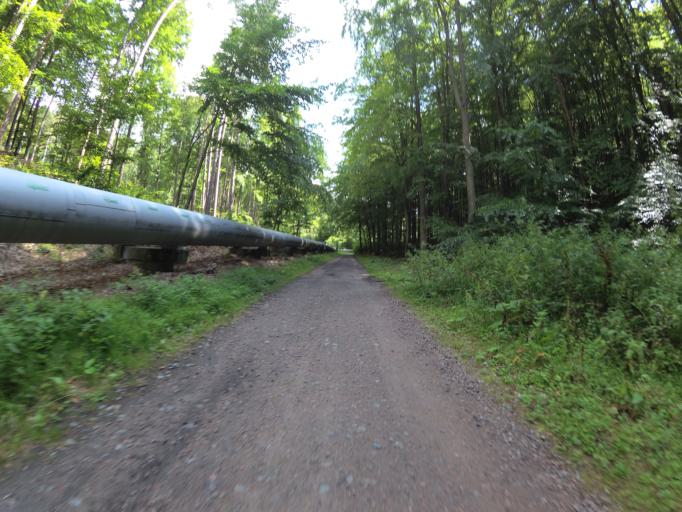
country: PL
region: Pomeranian Voivodeship
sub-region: Gdynia
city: Wielki Kack
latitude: 54.5117
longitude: 18.4831
